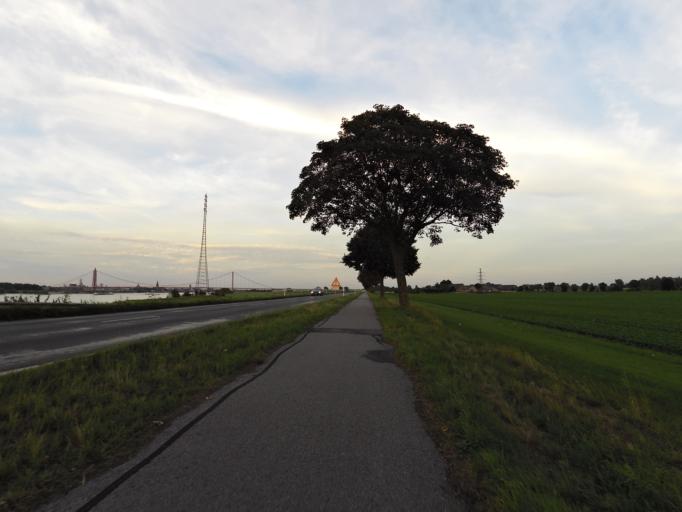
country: DE
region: North Rhine-Westphalia
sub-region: Regierungsbezirk Dusseldorf
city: Emmerich
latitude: 51.8263
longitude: 6.2063
